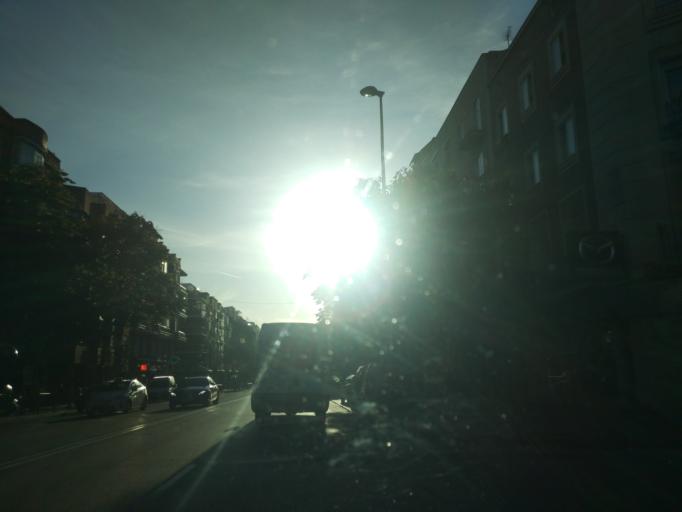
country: ES
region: Madrid
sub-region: Provincia de Madrid
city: Carabanchel
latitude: 40.3901
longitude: -3.7293
